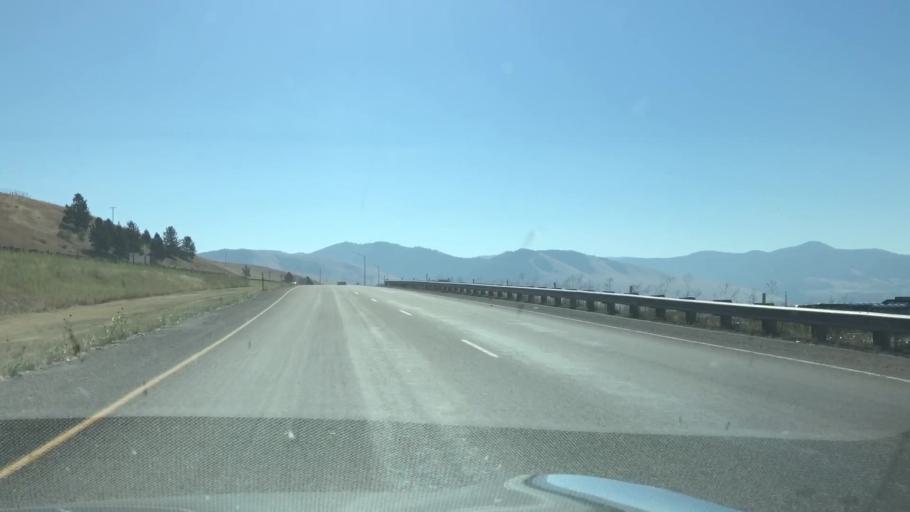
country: US
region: Montana
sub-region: Missoula County
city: Orchard Homes
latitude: 46.9115
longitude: -114.0331
